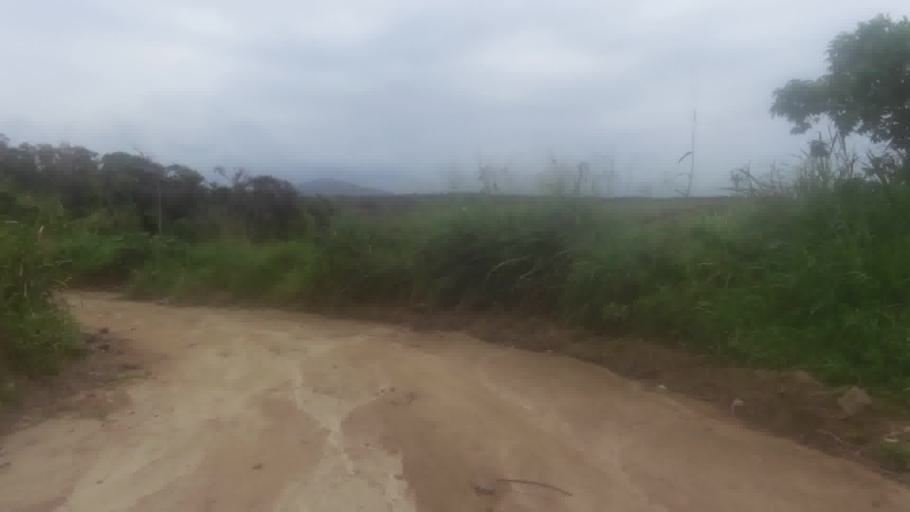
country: BR
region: Espirito Santo
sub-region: Piuma
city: Piuma
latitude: -20.7989
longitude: -40.5897
